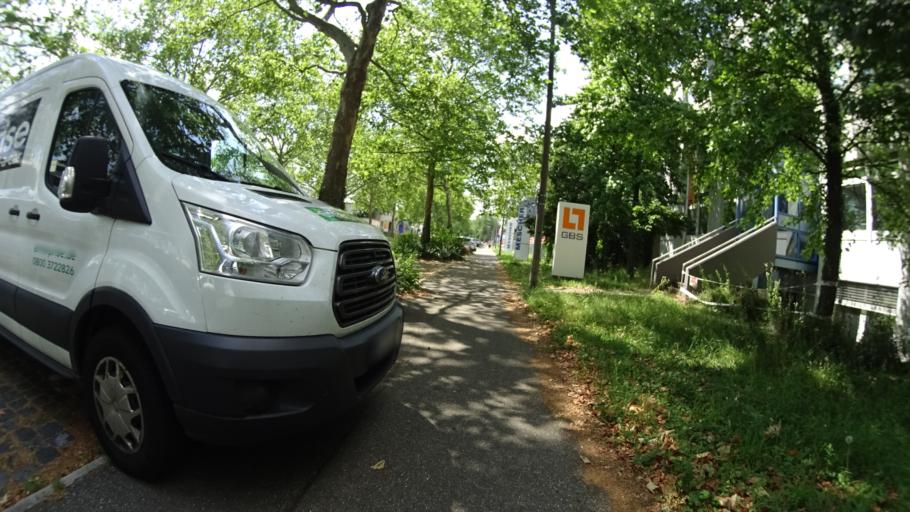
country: DE
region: Baden-Wuerttemberg
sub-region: Karlsruhe Region
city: Karlsruhe
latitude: 48.9962
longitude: 8.4482
